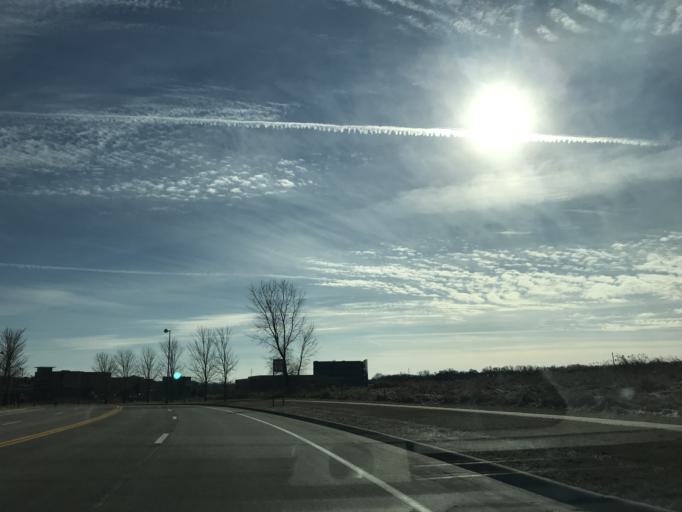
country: US
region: Wisconsin
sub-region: Dane County
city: Windsor
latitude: 43.1476
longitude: -89.2992
